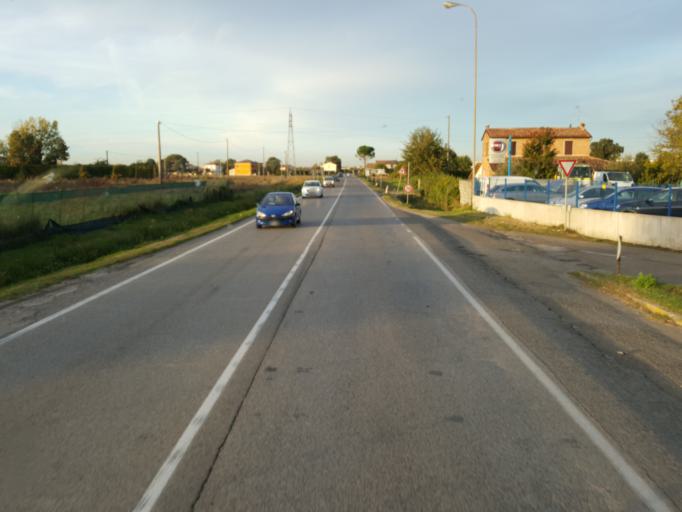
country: IT
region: Emilia-Romagna
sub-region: Provincia di Ravenna
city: Faenza
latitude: 44.3035
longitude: 11.8854
